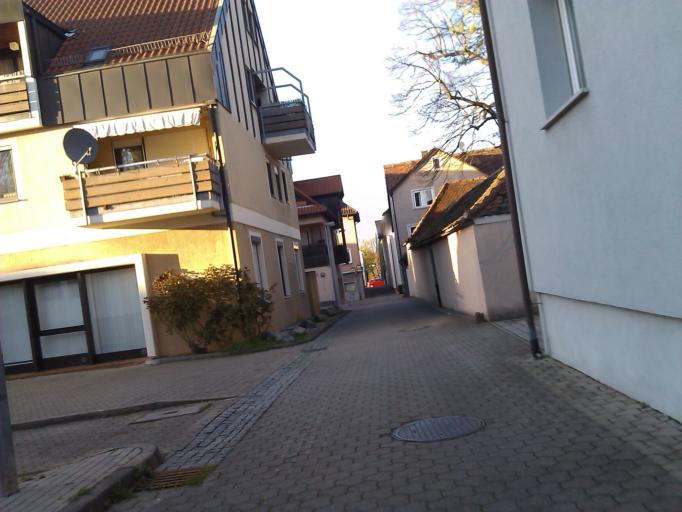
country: DE
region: Baden-Wuerttemberg
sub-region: Regierungsbezirk Stuttgart
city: Neckarsulm
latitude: 49.1902
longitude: 9.2273
